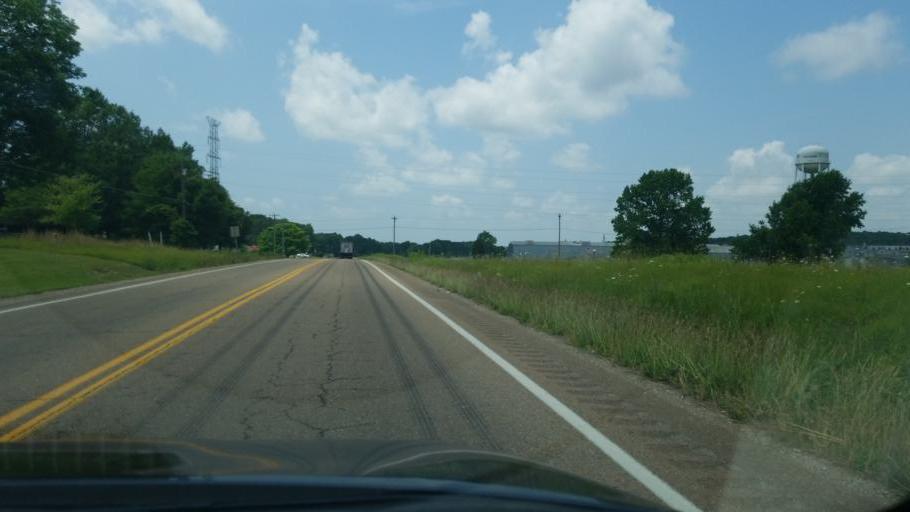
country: US
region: Tennessee
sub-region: Carroll County
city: Huntingdon
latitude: 36.0187
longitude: -88.3761
